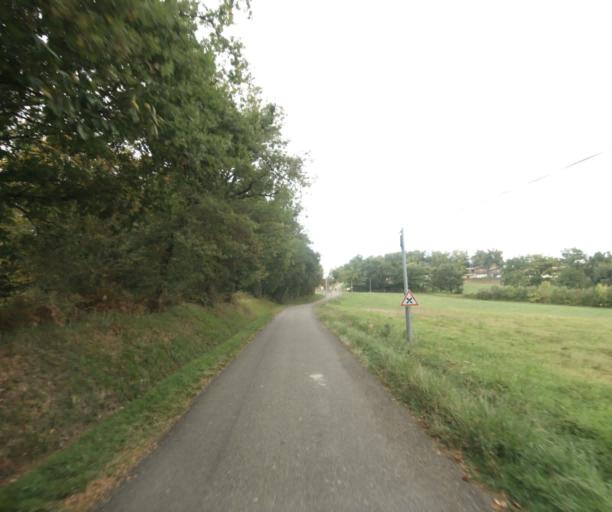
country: FR
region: Midi-Pyrenees
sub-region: Departement du Gers
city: Eauze
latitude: 43.8988
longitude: 0.1107
